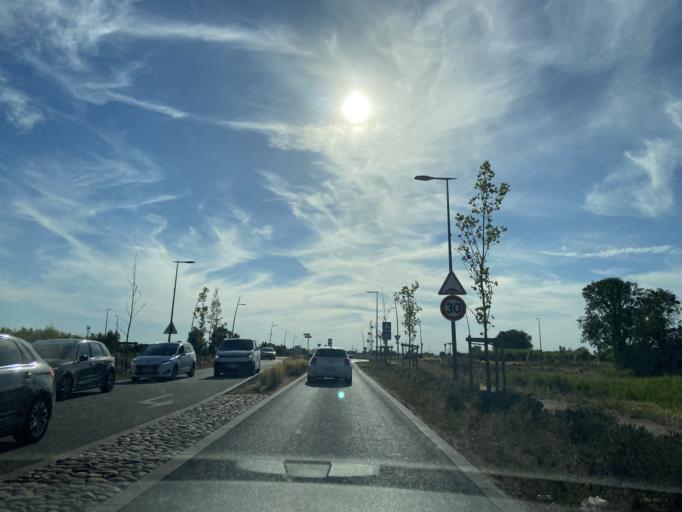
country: FR
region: Provence-Alpes-Cote d'Azur
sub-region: Departement des Bouches-du-Rhone
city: Miramas
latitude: 43.5884
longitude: 4.9938
